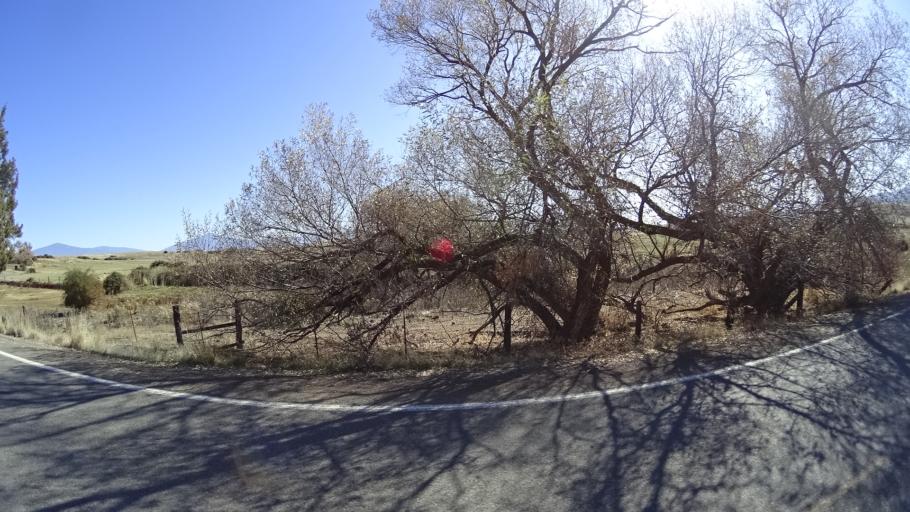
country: US
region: California
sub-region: Siskiyou County
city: Montague
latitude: 41.7491
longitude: -122.5709
